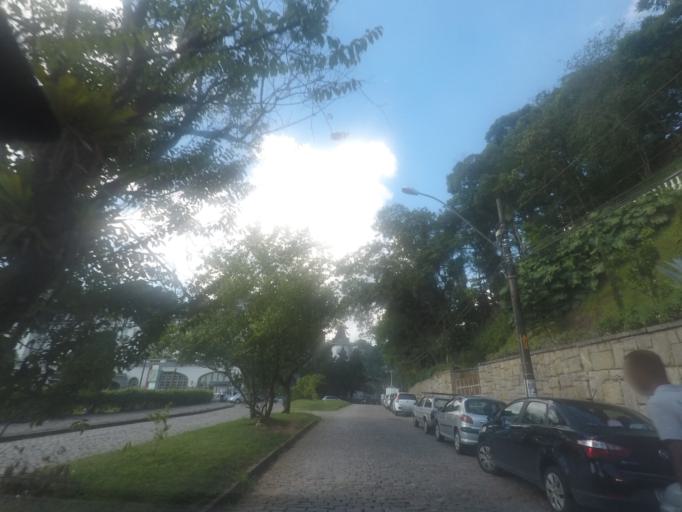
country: BR
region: Rio de Janeiro
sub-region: Petropolis
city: Petropolis
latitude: -22.5284
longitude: -43.2120
